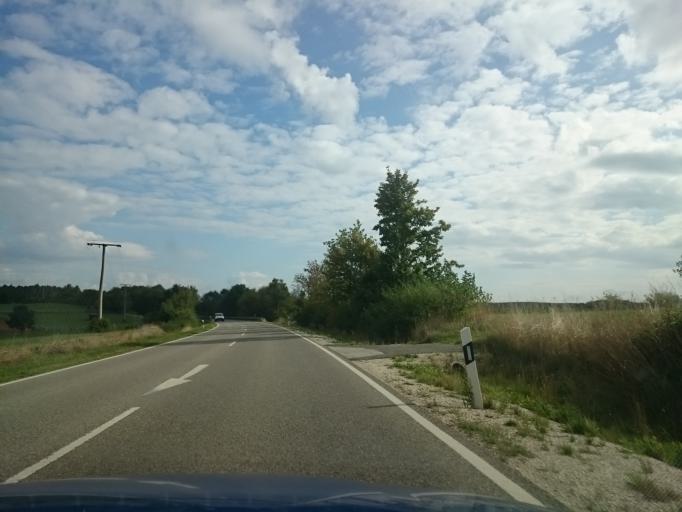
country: DE
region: Bavaria
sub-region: Regierungsbezirk Mittelfranken
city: Allersberg
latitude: 49.2350
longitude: 11.2116
